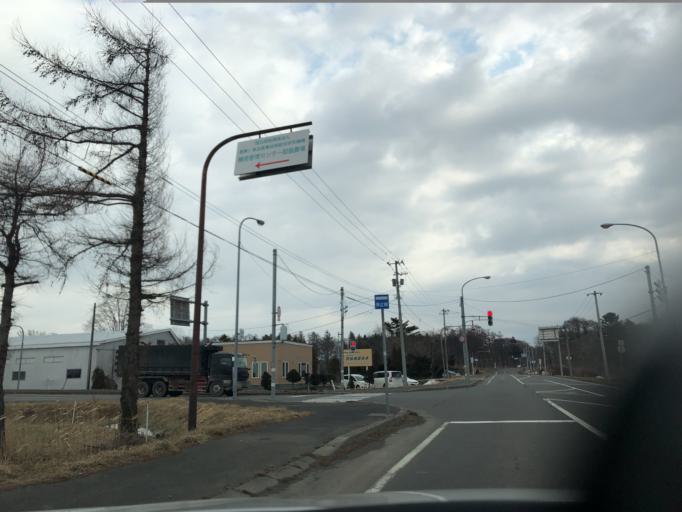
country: JP
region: Hokkaido
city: Chitose
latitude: 42.7617
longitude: 141.7732
